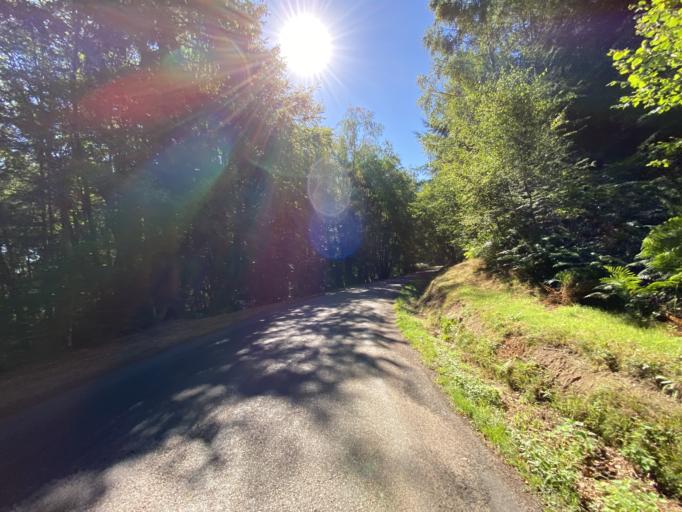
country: FR
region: Bourgogne
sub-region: Departement de la Cote-d'Or
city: Saulieu
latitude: 47.2763
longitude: 4.1644
